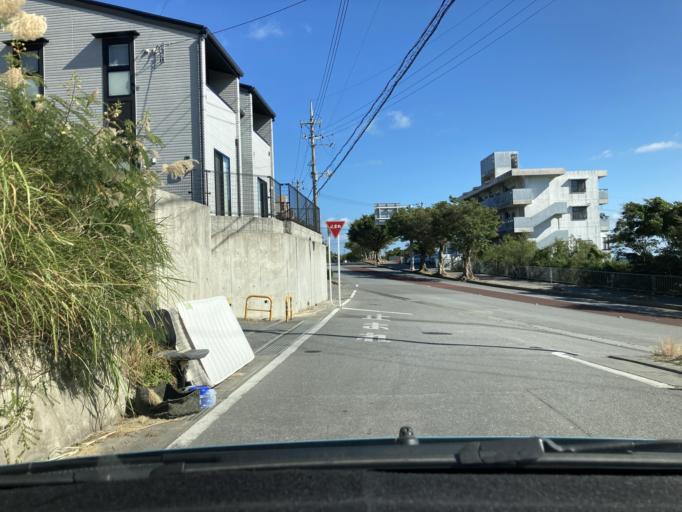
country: JP
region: Okinawa
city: Gushikawa
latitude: 26.3520
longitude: 127.8395
